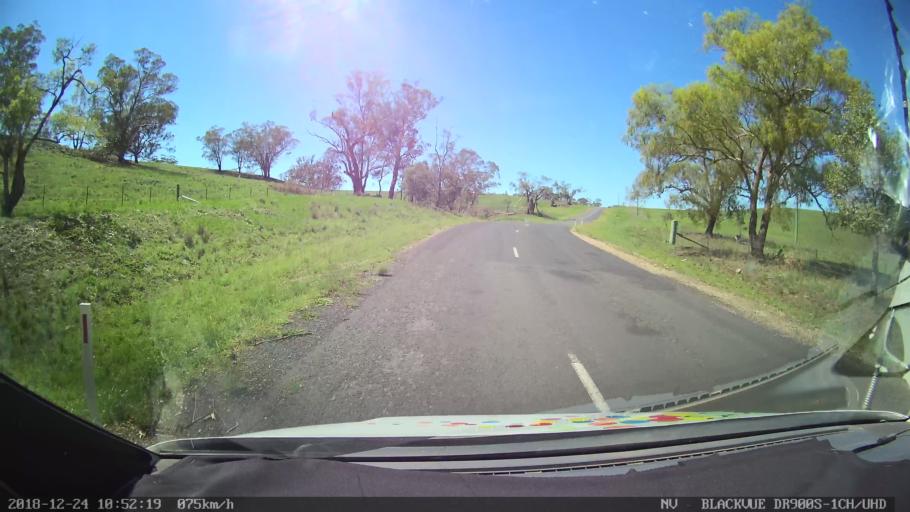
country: AU
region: New South Wales
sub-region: Upper Hunter Shire
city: Merriwa
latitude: -31.9792
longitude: 150.4218
